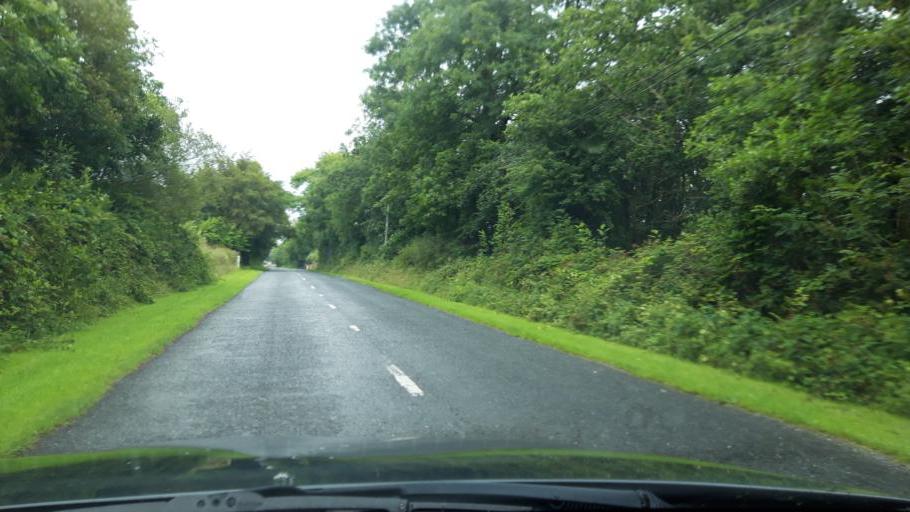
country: IE
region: Munster
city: Cahir
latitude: 52.1788
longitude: -7.8495
